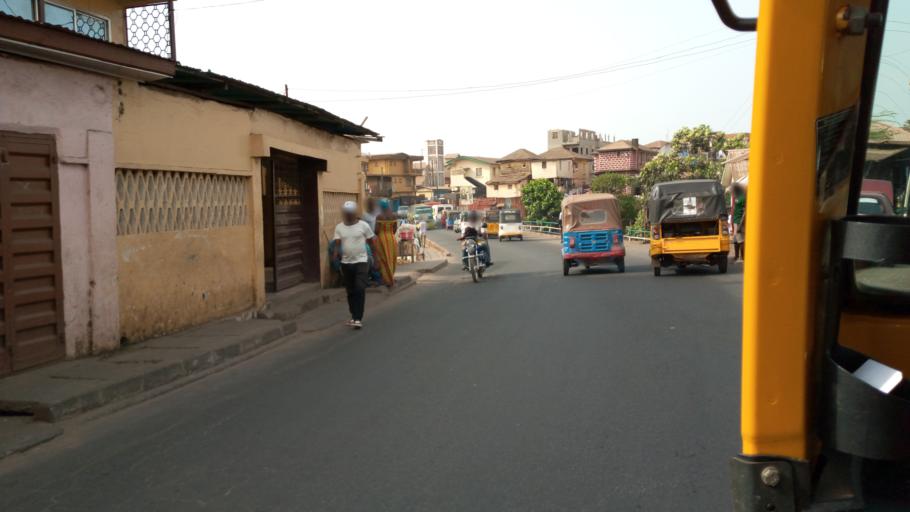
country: SL
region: Western Area
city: Freetown
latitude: 8.4774
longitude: -13.2434
